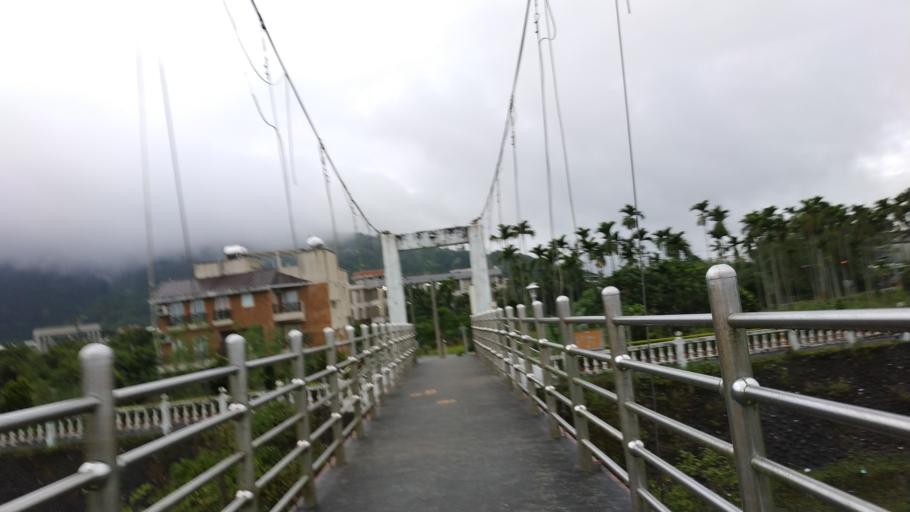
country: TW
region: Taiwan
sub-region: Hualien
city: Hualian
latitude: 23.6624
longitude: 121.4245
